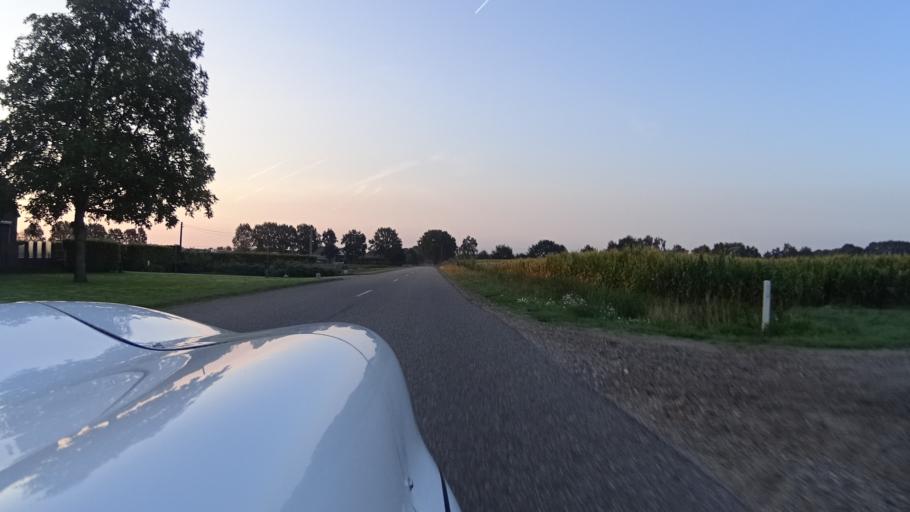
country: NL
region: North Brabant
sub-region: Gemeente Mill en Sint Hubert
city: Wilbertoord
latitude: 51.6016
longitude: 5.7871
